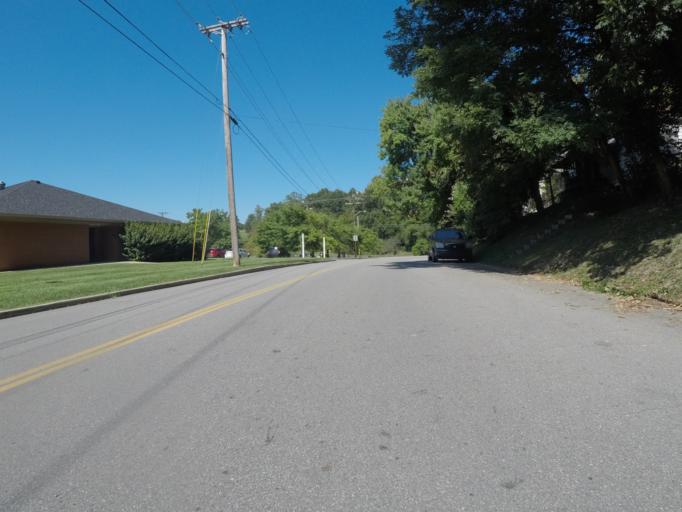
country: US
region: Kentucky
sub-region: Boyd County
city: Ashland
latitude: 38.4682
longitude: -82.6470
